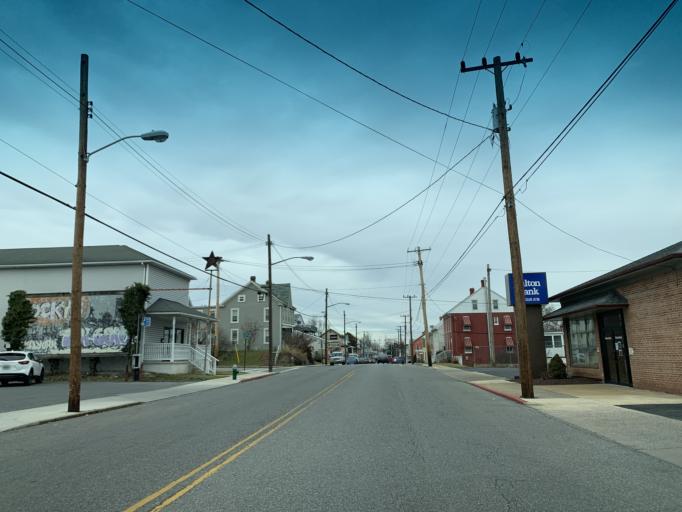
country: US
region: Maryland
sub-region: Washington County
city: Hagerstown
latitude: 39.6255
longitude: -77.7273
